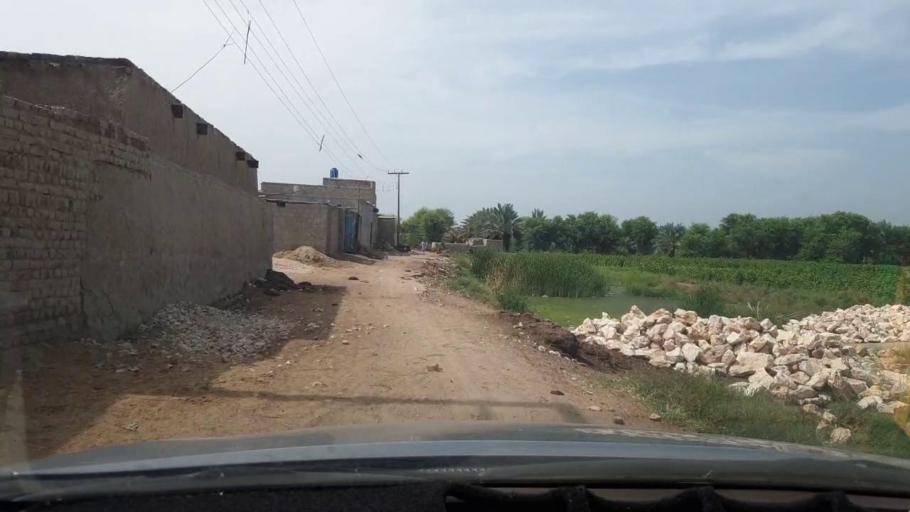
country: PK
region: Sindh
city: Khairpur
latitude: 27.4992
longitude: 68.7547
